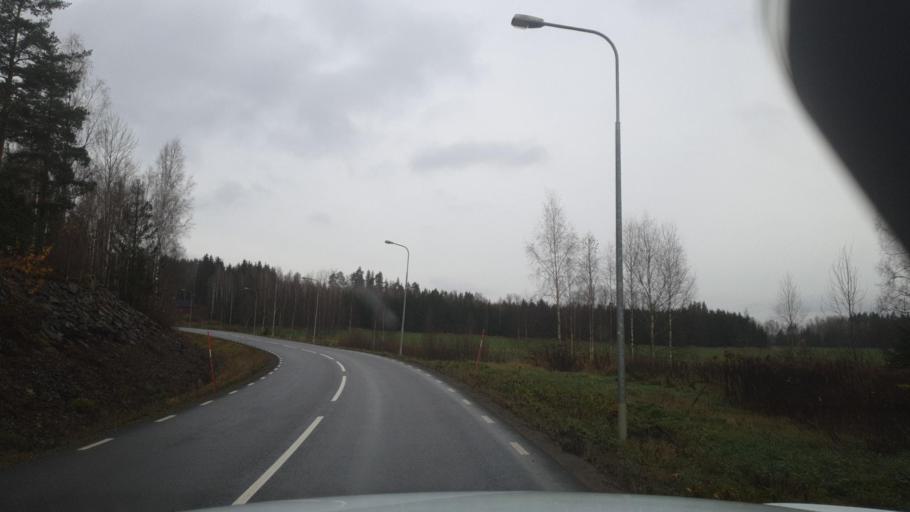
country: SE
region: Vaermland
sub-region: Arvika Kommun
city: Arvika
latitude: 59.5359
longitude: 12.5948
